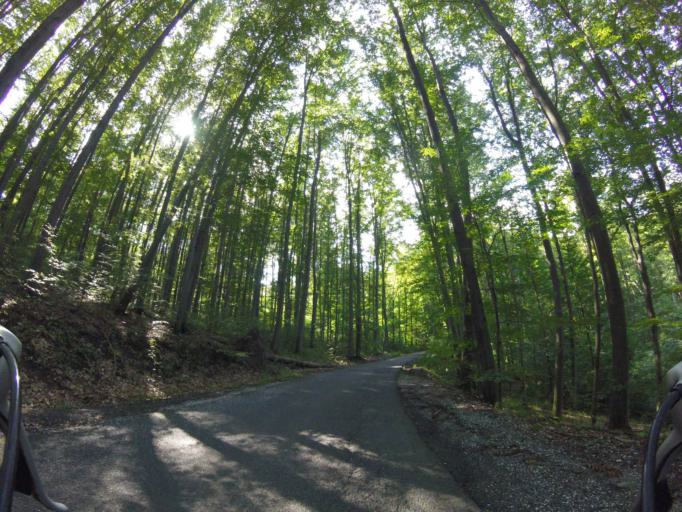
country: HU
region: Borsod-Abauj-Zemplen
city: Sajobabony
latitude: 48.1095
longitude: 20.6062
